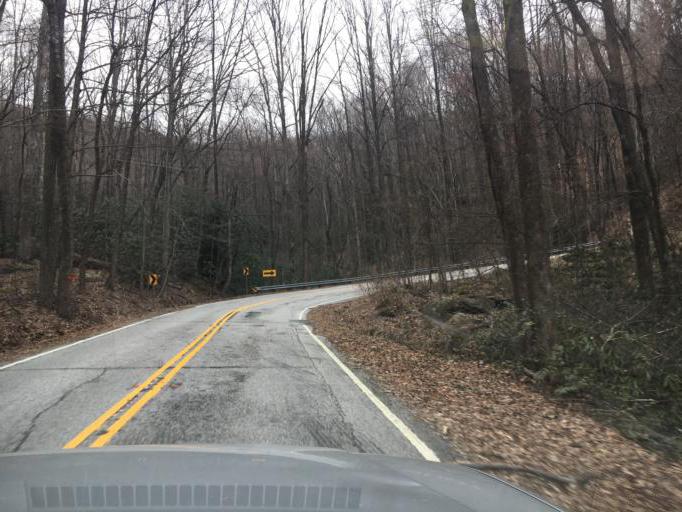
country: US
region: South Carolina
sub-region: Greenville County
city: Slater-Marietta
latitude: 35.1045
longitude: -82.6122
